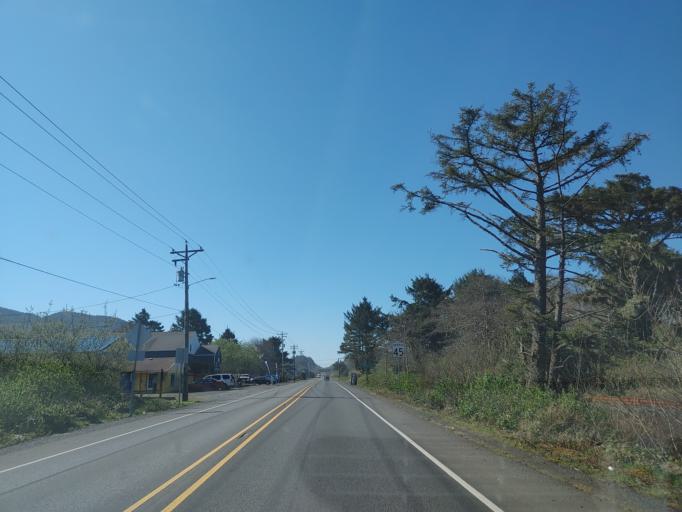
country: US
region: Oregon
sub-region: Tillamook County
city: Rockaway Beach
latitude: 45.5994
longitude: -123.9462
